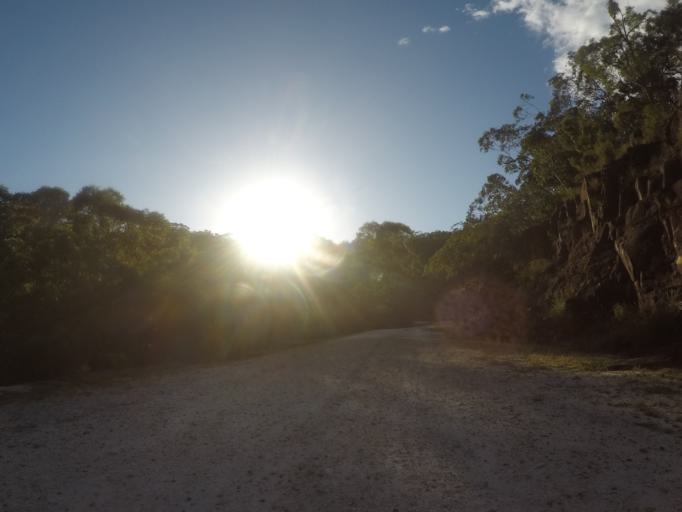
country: AU
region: New South Wales
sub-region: Hornsby Shire
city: Glenorie
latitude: -33.3687
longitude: 150.9859
